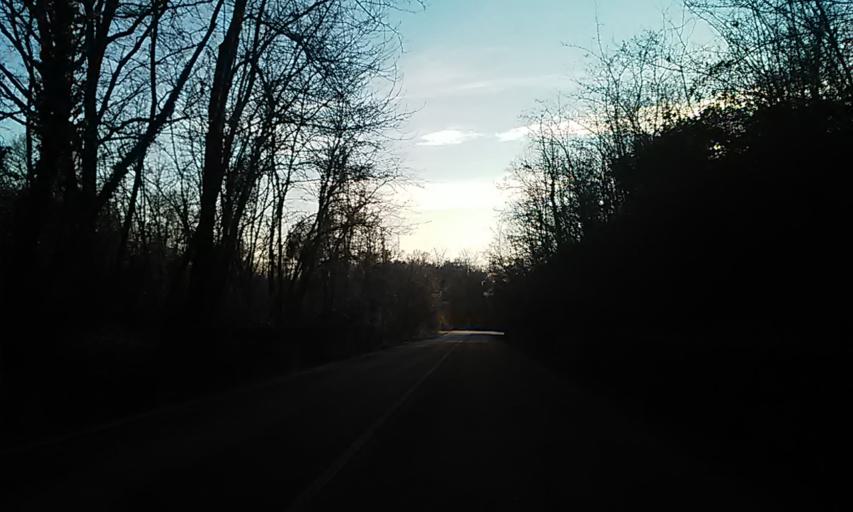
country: IT
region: Piedmont
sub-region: Provincia di Biella
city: Cossato
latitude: 45.5667
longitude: 8.2088
